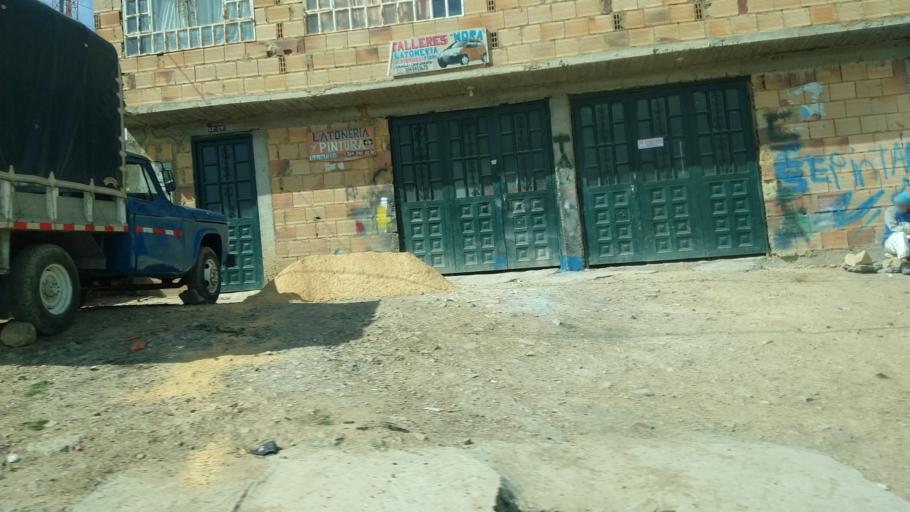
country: CO
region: Cundinamarca
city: Soacha
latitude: 4.5675
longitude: -74.1865
